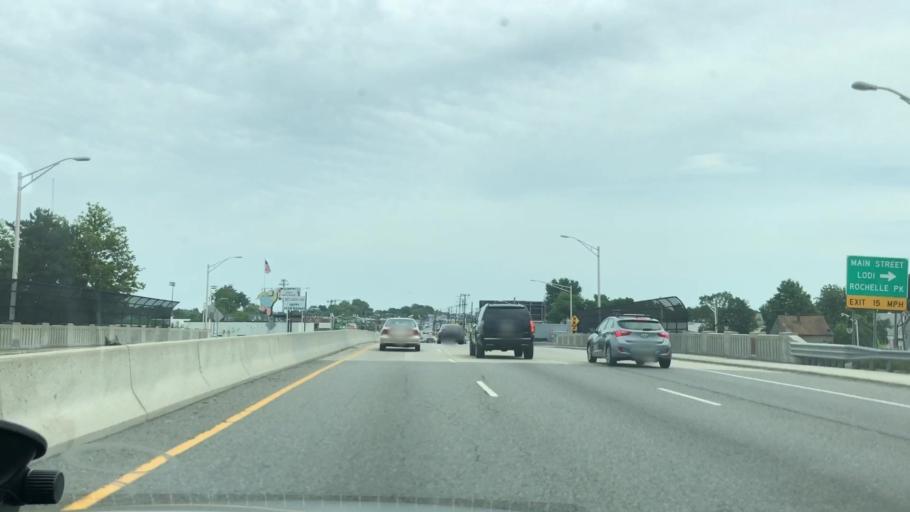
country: US
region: New Jersey
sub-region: Bergen County
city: Lodi
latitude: 40.8824
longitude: -74.0840
